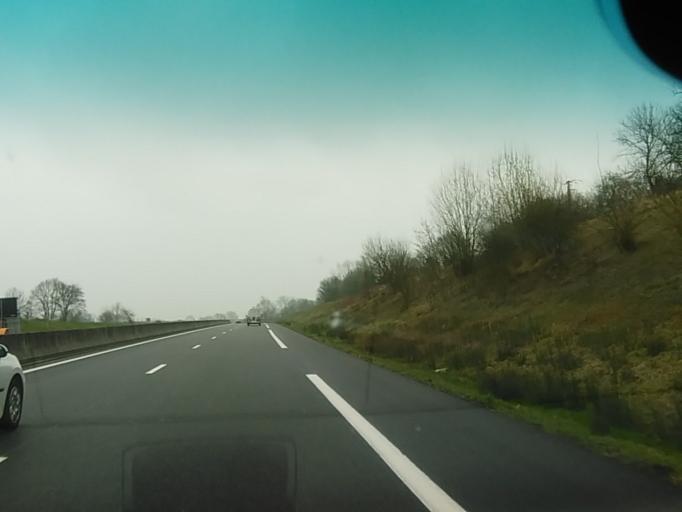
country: FR
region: Lower Normandy
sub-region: Departement de l'Orne
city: Gace
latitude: 48.7388
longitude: 0.2662
